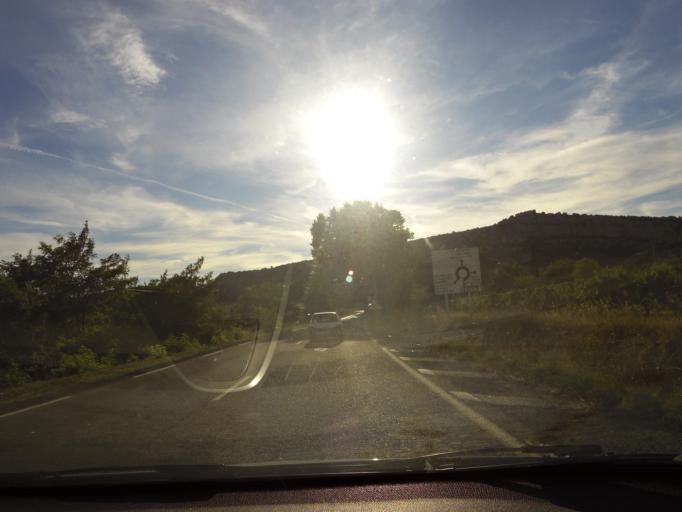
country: FR
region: Languedoc-Roussillon
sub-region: Departement de l'Herault
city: Claret
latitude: 43.8720
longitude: 3.9472
